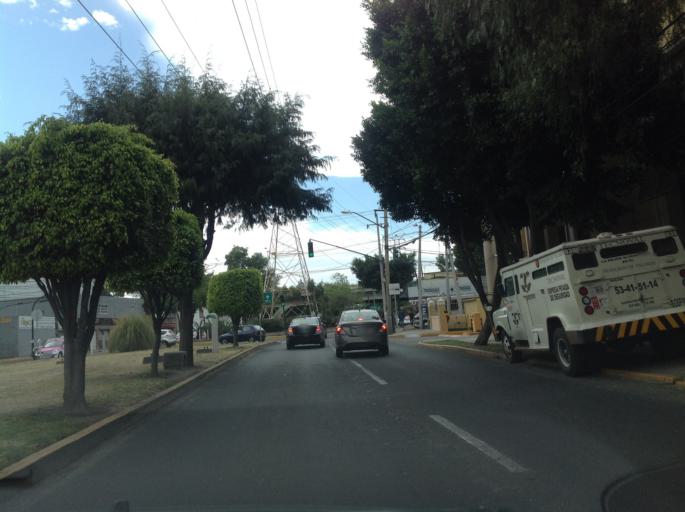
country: MX
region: Mexico City
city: Azcapotzalco
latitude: 19.4697
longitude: -99.1881
